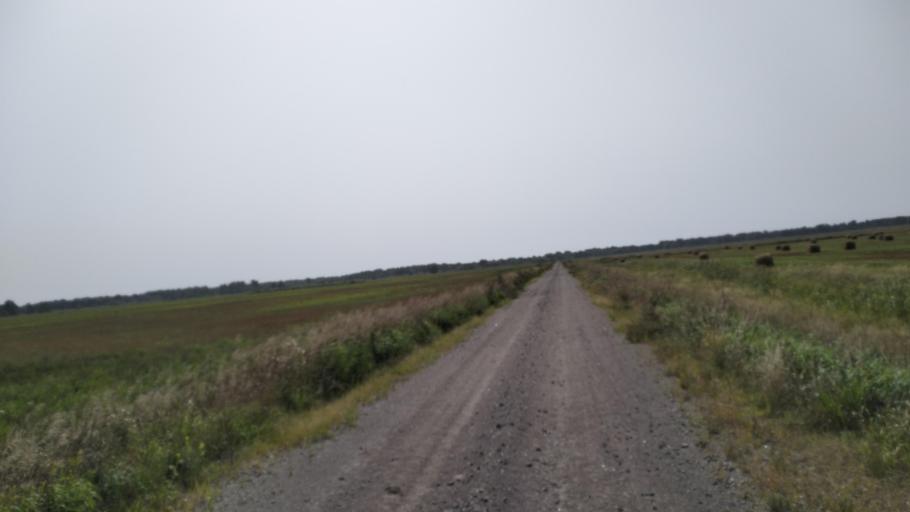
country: BY
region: Brest
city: Davyd-Haradok
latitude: 51.9796
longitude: 27.1749
